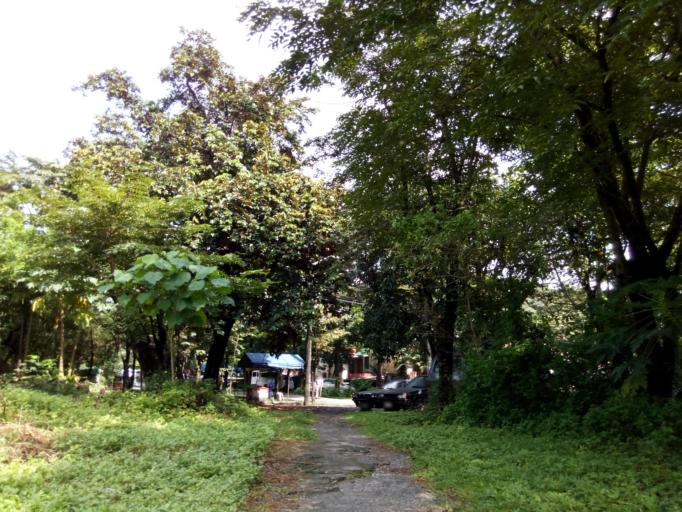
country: PH
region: Metro Manila
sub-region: Quezon City
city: Quezon City
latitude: 14.6444
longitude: 121.0698
